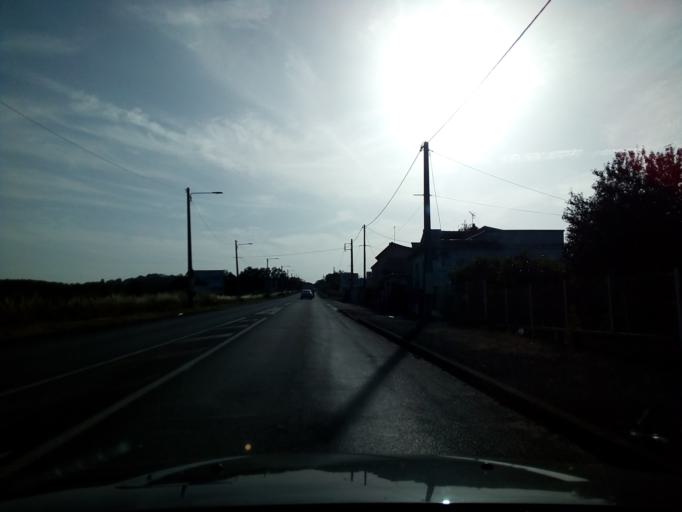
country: FR
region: Auvergne
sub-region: Departement de l'Allier
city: Premilhat
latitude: 46.3379
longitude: 2.5618
